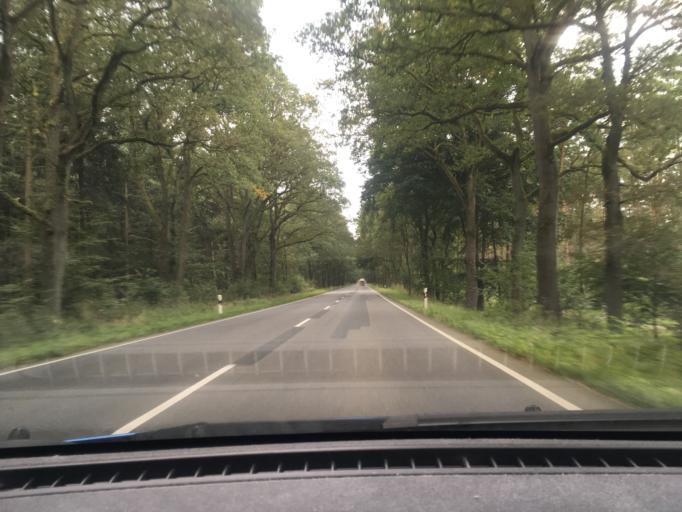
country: DE
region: Lower Saxony
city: Suderburg
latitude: 52.8510
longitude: 10.4902
